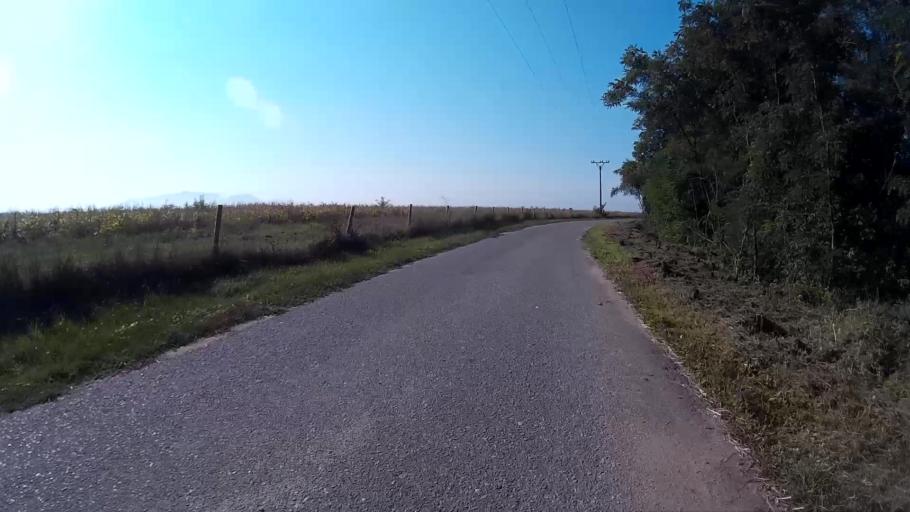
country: CZ
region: South Moravian
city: Vranovice
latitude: 48.9412
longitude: 16.5800
